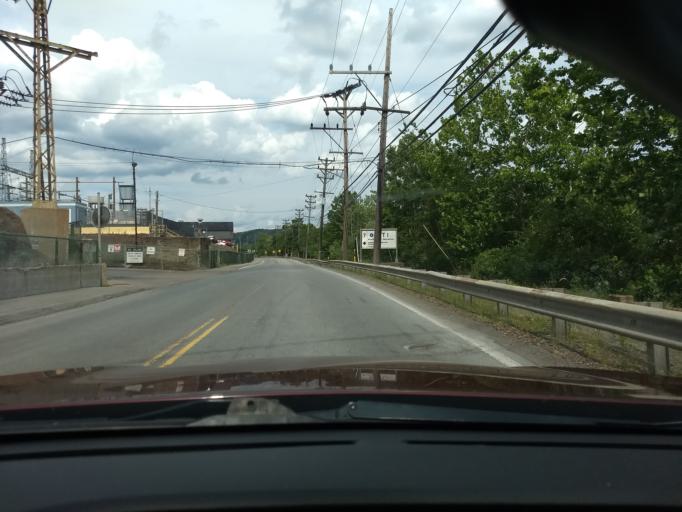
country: US
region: Pennsylvania
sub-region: Allegheny County
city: Brackenridge
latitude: 40.6071
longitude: -79.7256
